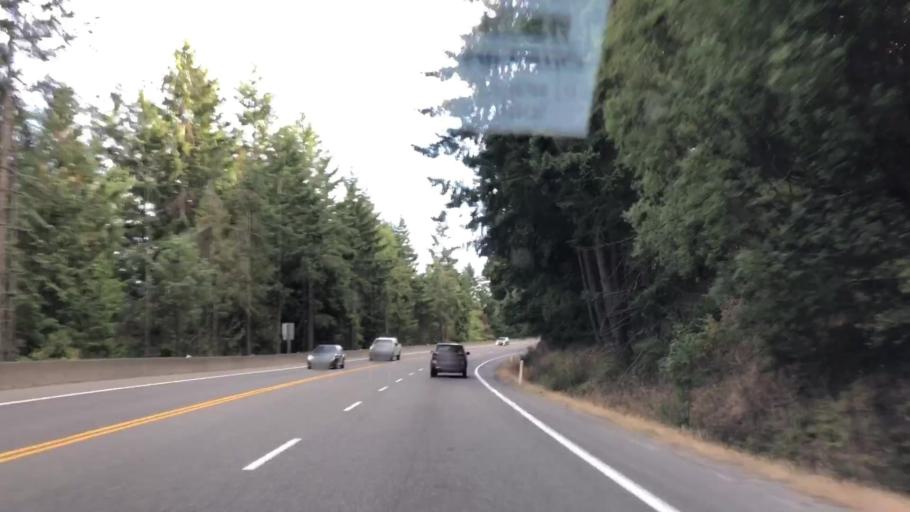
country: CA
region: British Columbia
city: Langford
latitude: 48.5751
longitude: -123.5269
